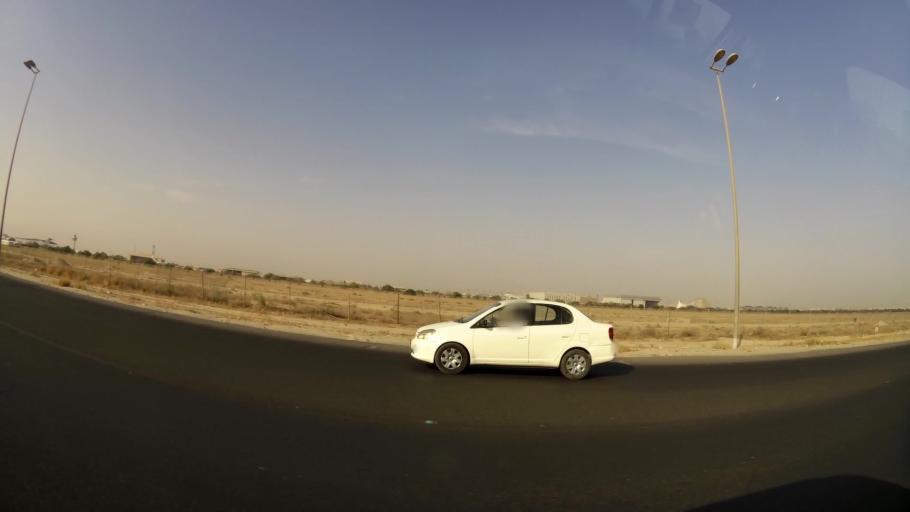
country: KW
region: Al Farwaniyah
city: Janub as Surrah
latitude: 29.2382
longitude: 47.9915
